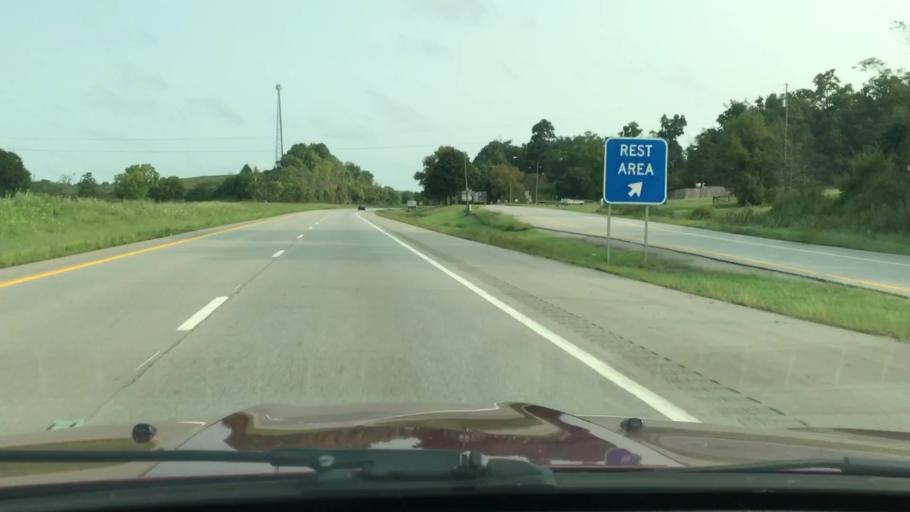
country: US
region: Ohio
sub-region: Guernsey County
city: Byesville
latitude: 39.9386
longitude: -81.5324
